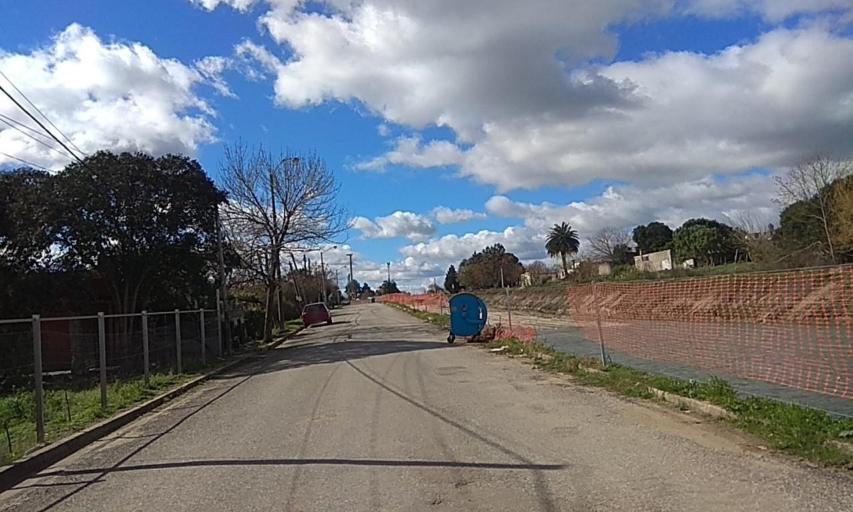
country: UY
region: Florida
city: Florida
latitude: -34.0919
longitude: -56.2228
